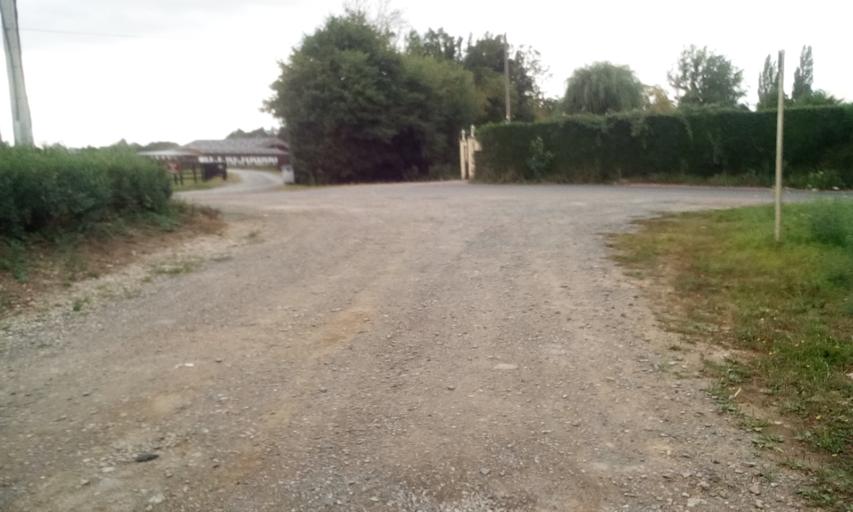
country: FR
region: Lower Normandy
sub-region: Departement du Calvados
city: Sannerville
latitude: 49.1858
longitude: -0.2150
